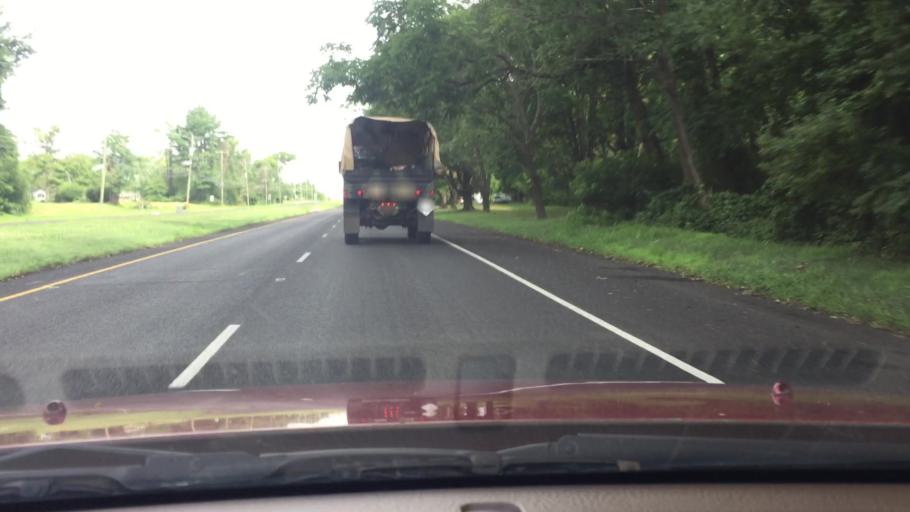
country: US
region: New Jersey
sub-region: Burlington County
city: Bordentown
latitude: 40.1005
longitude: -74.6894
